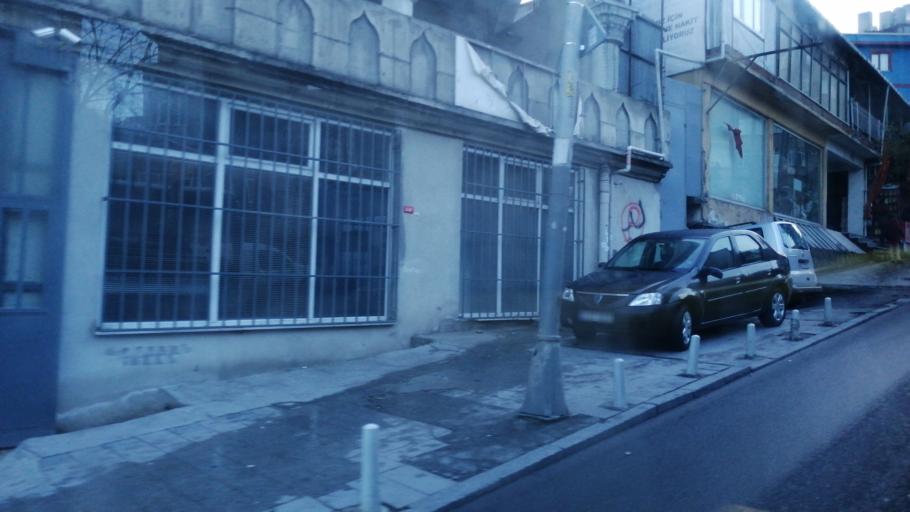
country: TR
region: Istanbul
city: Sisli
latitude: 41.0851
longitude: 28.9877
